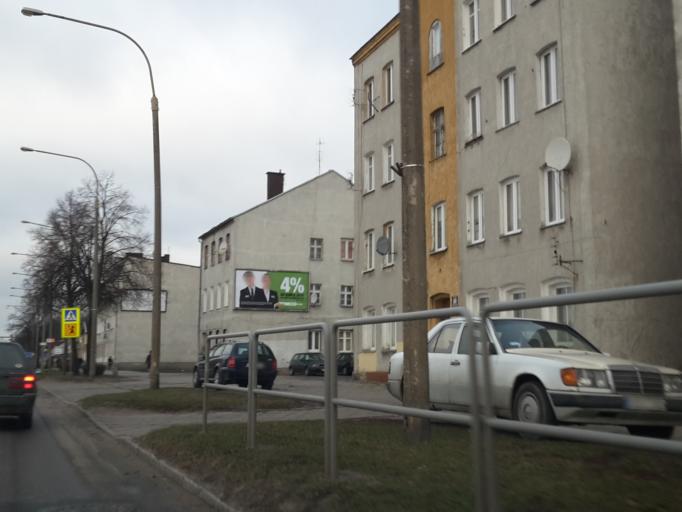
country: PL
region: Warmian-Masurian Voivodeship
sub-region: Powiat elblaski
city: Elblag
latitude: 54.1500
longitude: 19.4246
